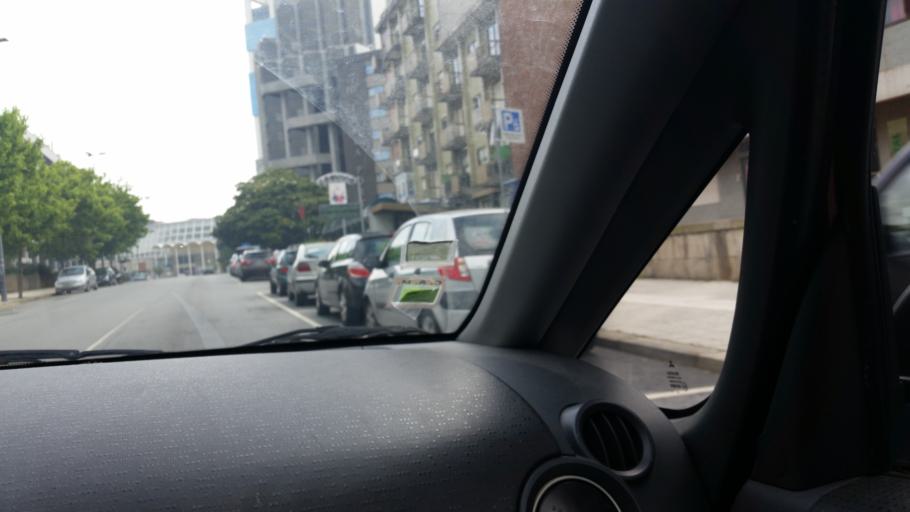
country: PT
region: Porto
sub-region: Porto
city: Porto
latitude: 41.1542
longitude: -8.6316
